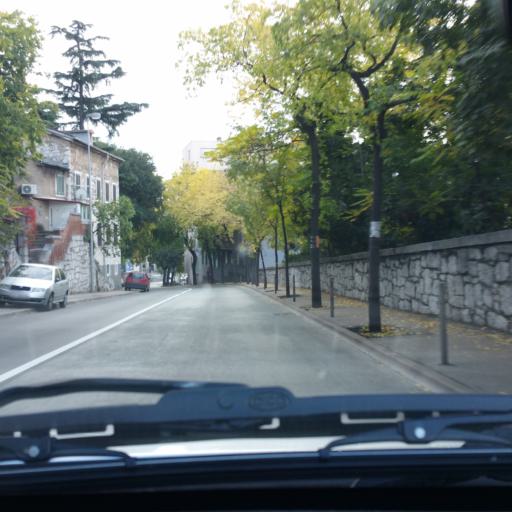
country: HR
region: Primorsko-Goranska
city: Drenova
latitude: 45.3332
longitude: 14.4333
